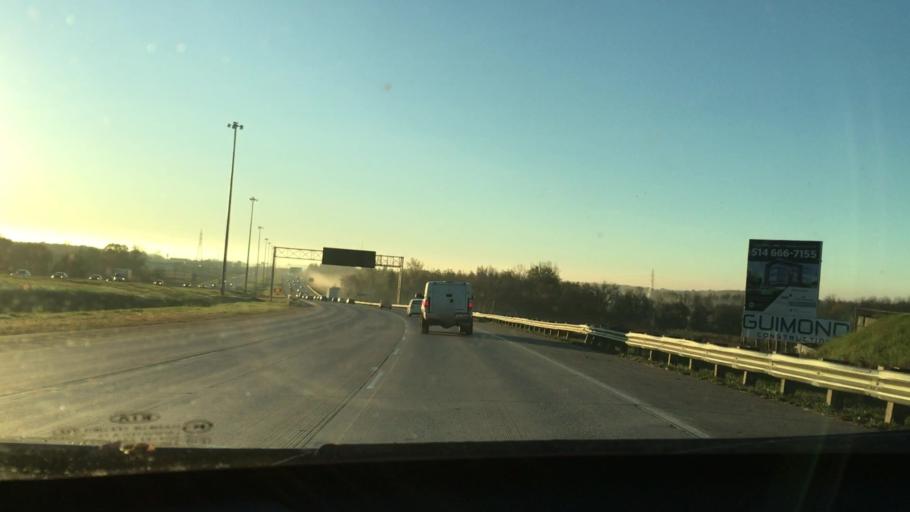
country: CA
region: Quebec
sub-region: Laurentides
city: Saint-Jerome
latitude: 45.7552
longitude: -74.0186
